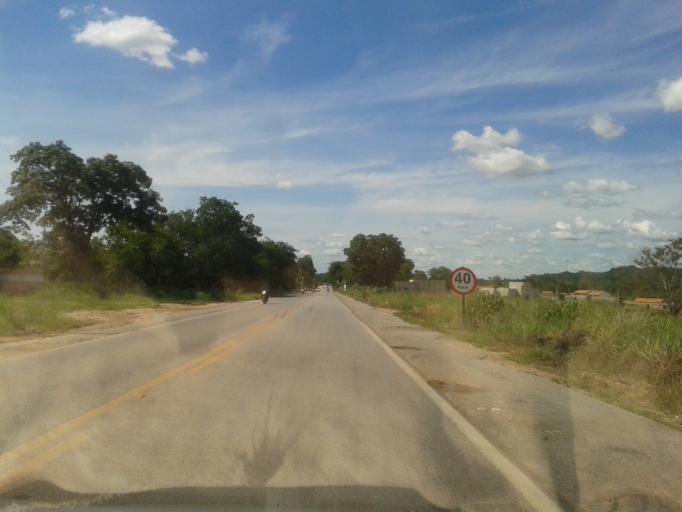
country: BR
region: Goias
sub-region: Itapuranga
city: Itapuranga
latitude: -15.4450
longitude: -50.3651
